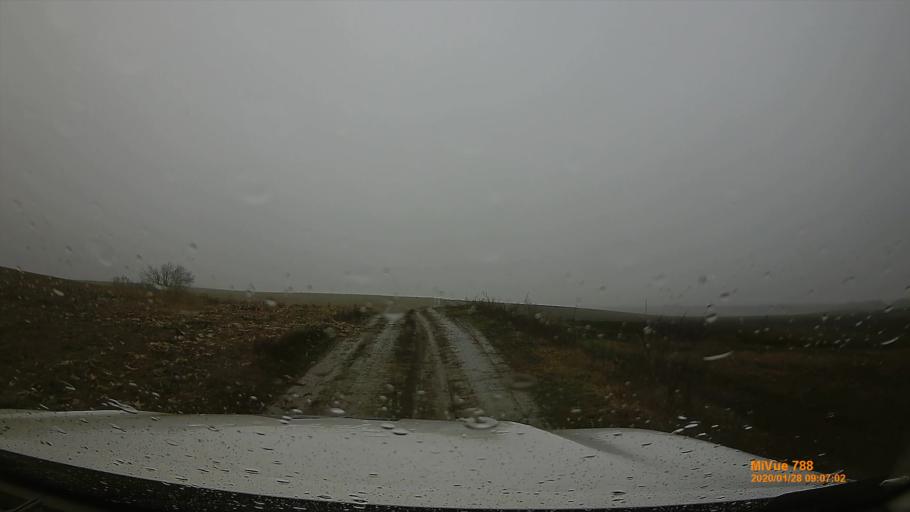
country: HU
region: Pest
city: Pilis
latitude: 47.3177
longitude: 19.5384
